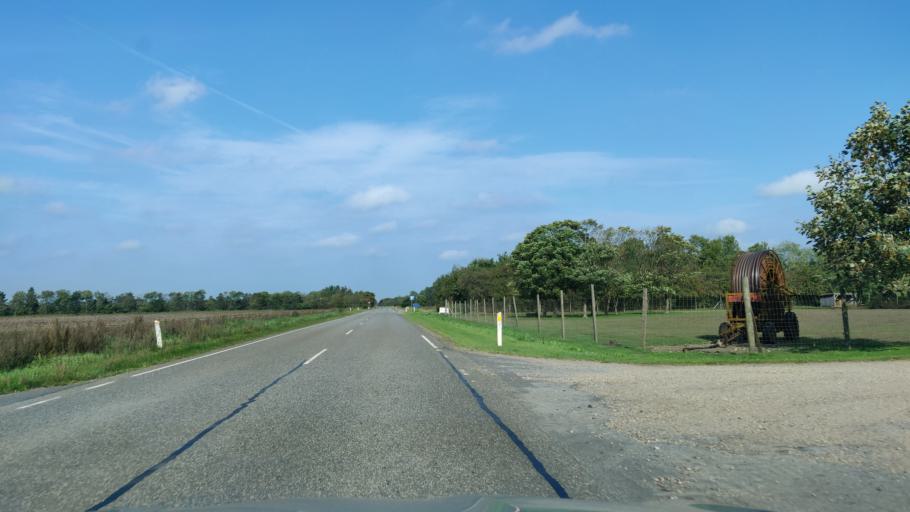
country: DK
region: Central Jutland
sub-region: Herning Kommune
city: Sunds
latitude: 56.2526
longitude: 9.0528
